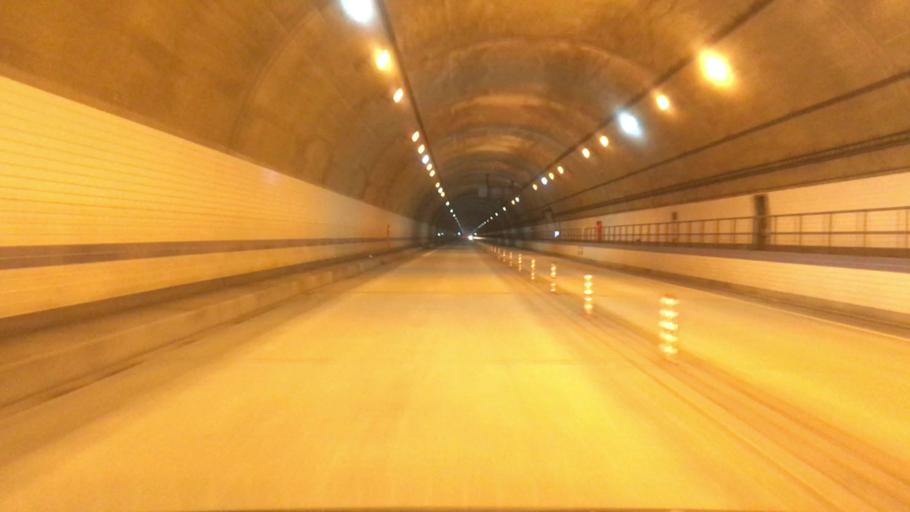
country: JP
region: Hyogo
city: Toyooka
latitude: 35.6295
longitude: 134.6004
